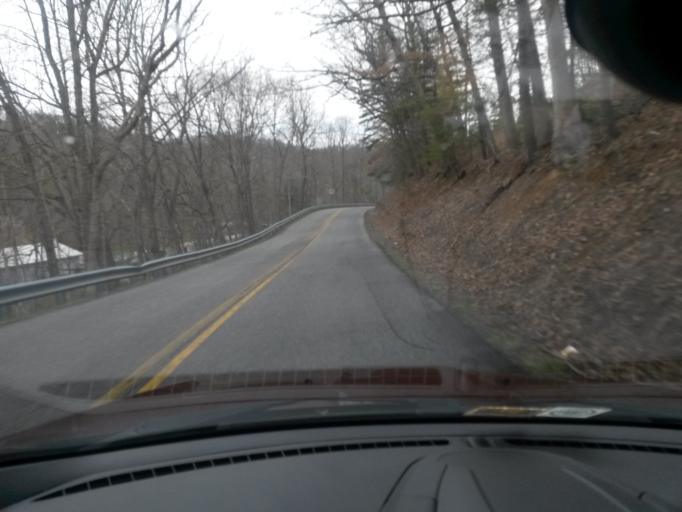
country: US
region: Virginia
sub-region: Bath County
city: Warm Springs
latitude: 38.0028
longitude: -79.8779
